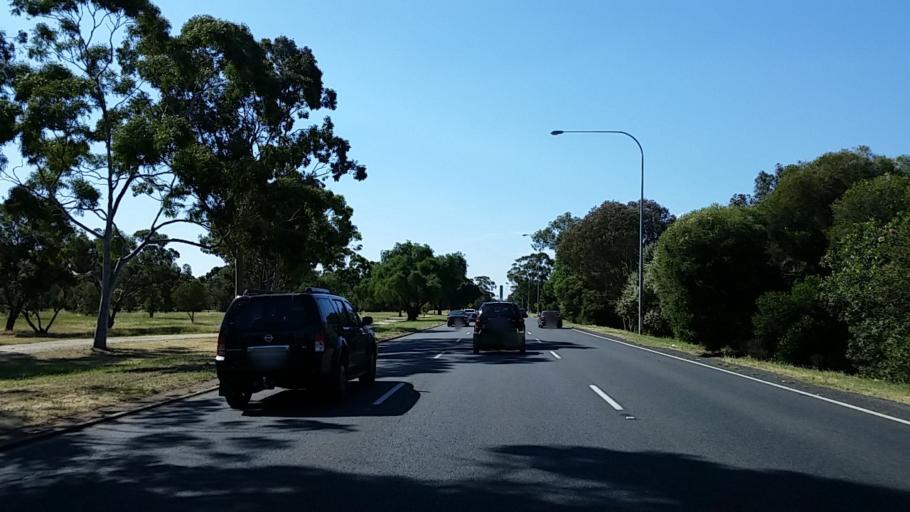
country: AU
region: South Australia
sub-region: Salisbury
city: Elizabeth
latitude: -34.7265
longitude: 138.6745
